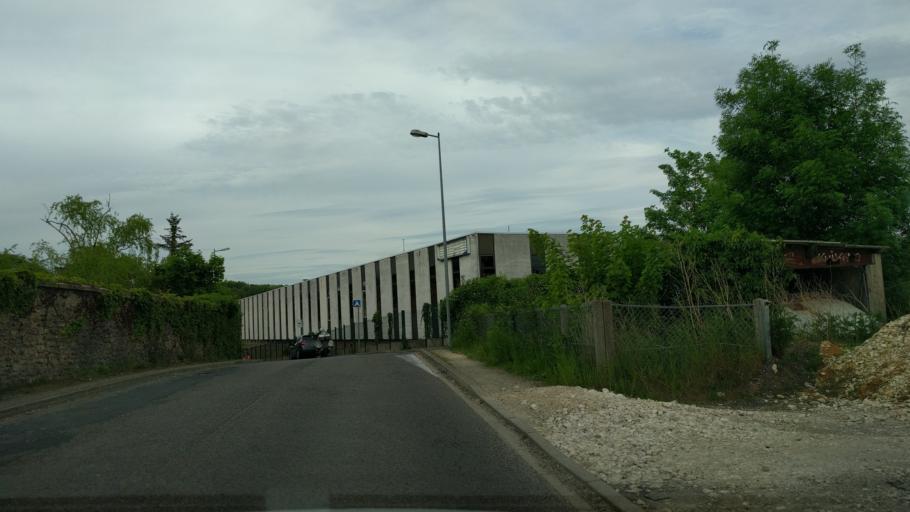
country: FR
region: Ile-de-France
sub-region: Departement de Seine-et-Marne
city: Ponthierry
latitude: 48.5363
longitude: 2.5415
